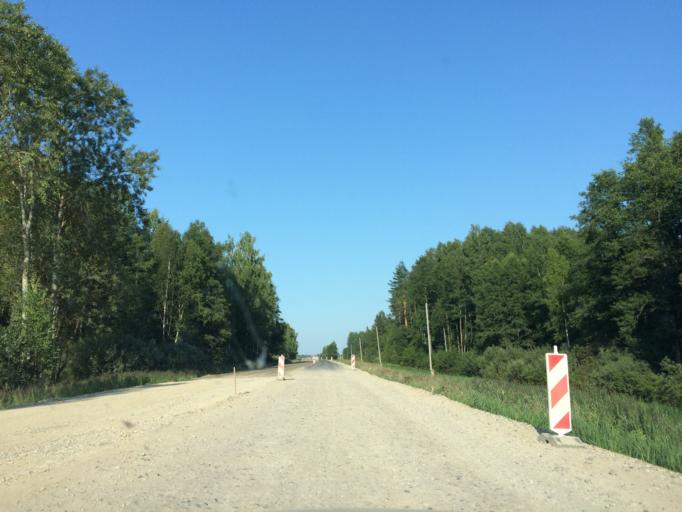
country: LV
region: Rezekne
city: Rezekne
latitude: 56.5146
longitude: 27.4875
